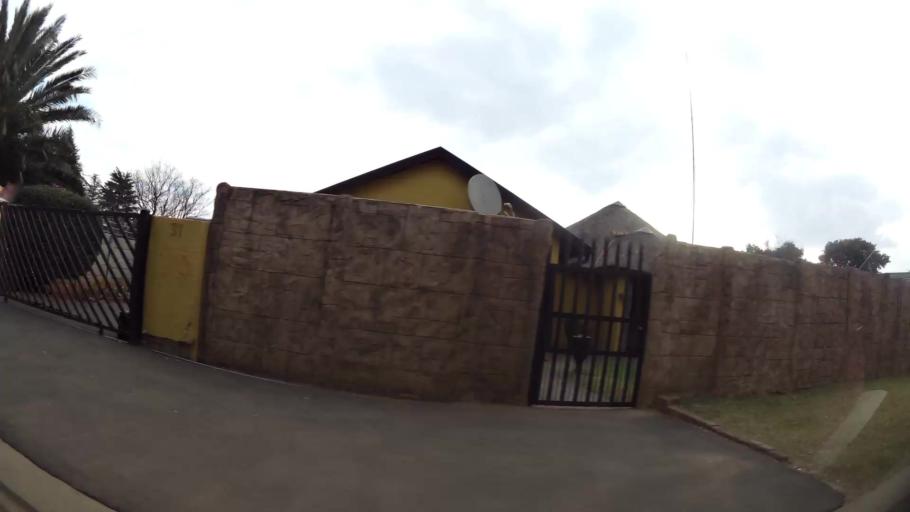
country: ZA
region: Gauteng
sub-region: Ekurhuleni Metropolitan Municipality
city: Benoni
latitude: -26.1333
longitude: 28.3597
